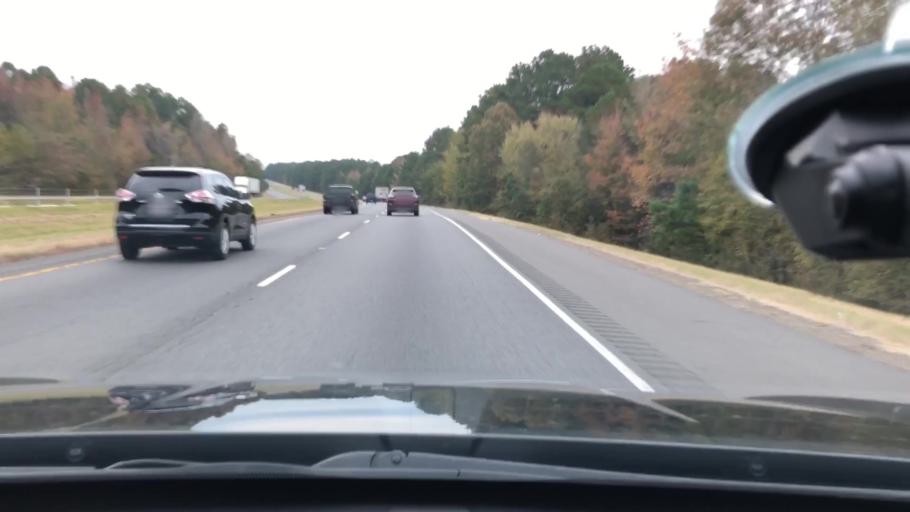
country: US
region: Arkansas
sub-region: Clark County
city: Gurdon
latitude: 34.0341
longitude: -93.1451
